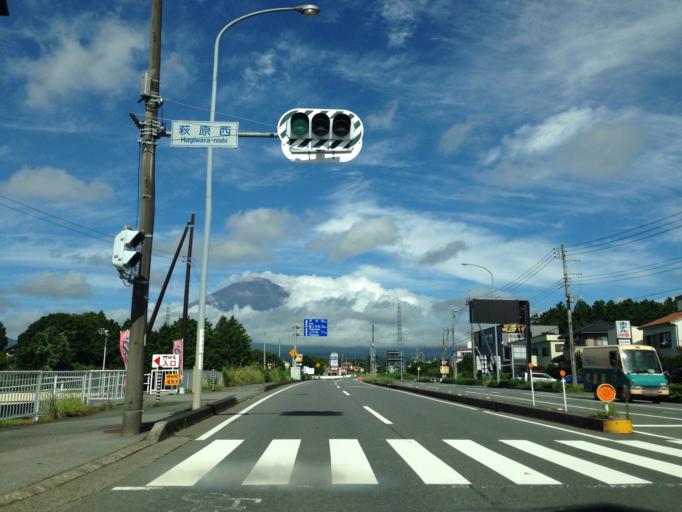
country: JP
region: Shizuoka
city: Gotemba
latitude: 35.3131
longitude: 138.9265
